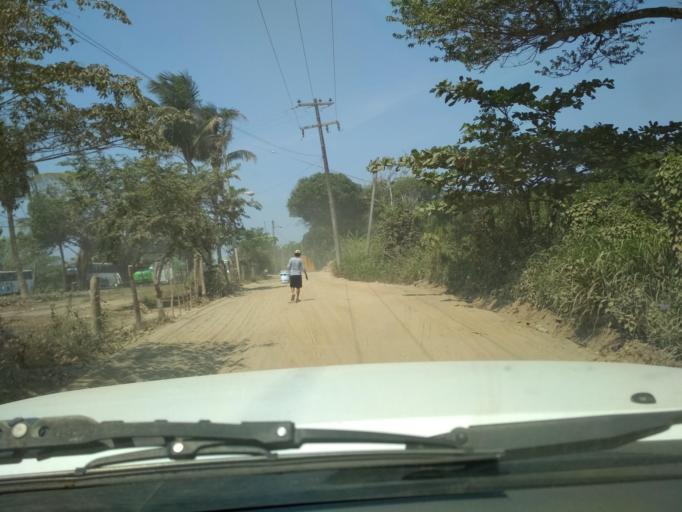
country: MX
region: Veracruz
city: Boca del Rio
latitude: 19.0975
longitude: -96.1244
